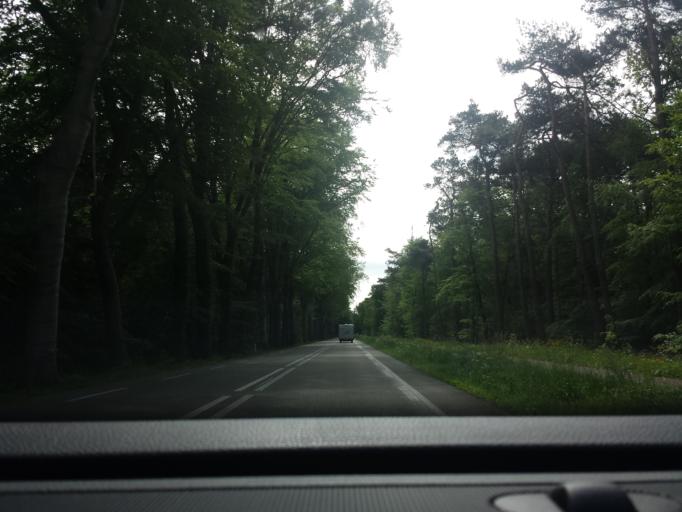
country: NL
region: Gelderland
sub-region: Gemeente Lochem
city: Barchem
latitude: 52.0915
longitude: 6.4058
